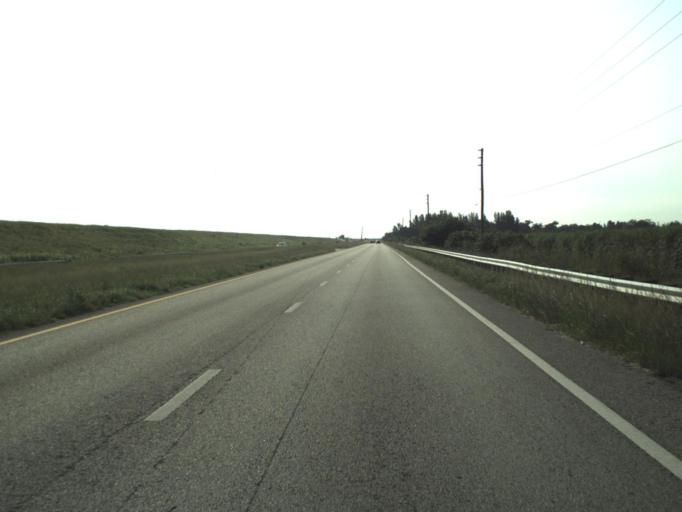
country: US
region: Florida
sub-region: Hendry County
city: Clewiston
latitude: 26.7358
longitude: -80.8695
